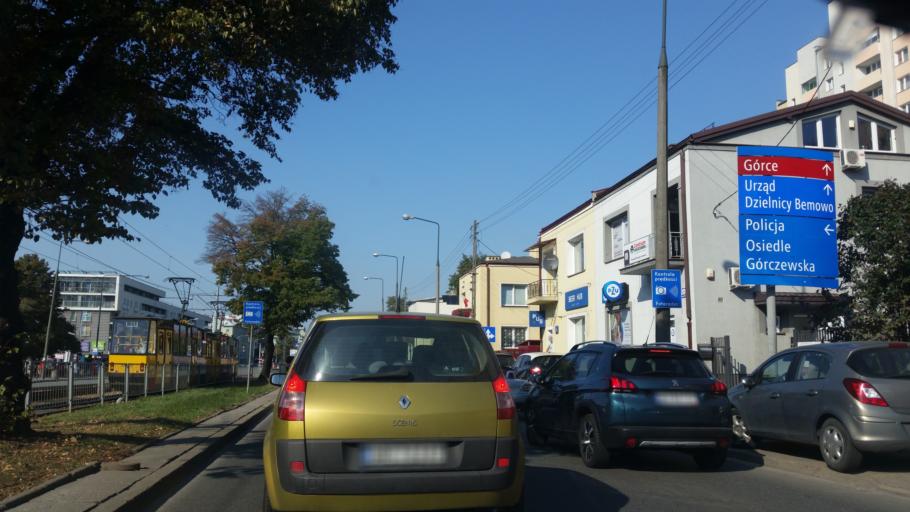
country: PL
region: Masovian Voivodeship
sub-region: Warszawa
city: Bemowo
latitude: 52.2278
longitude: 20.9158
